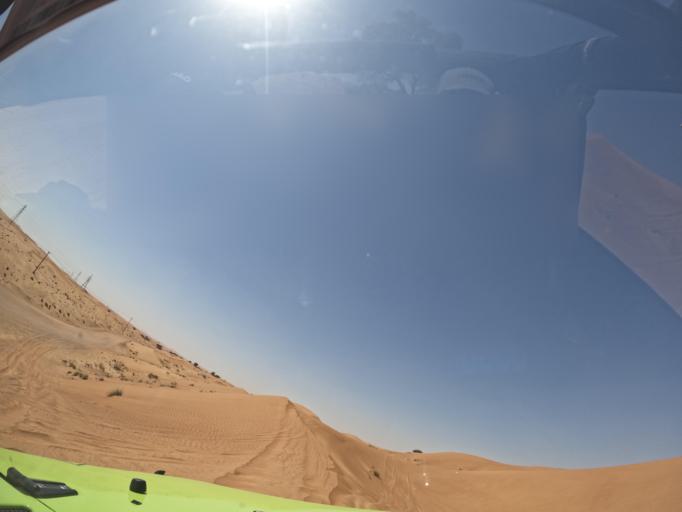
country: AE
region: Ash Shariqah
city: Adh Dhayd
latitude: 25.0211
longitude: 55.7519
